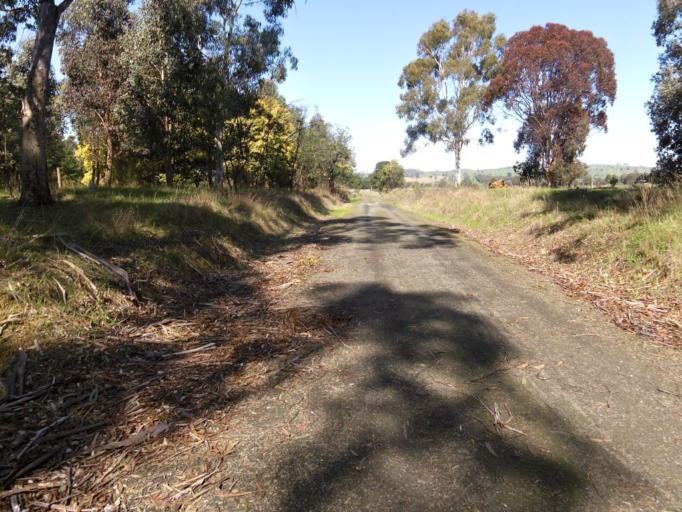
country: AU
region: Victoria
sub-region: Murrindindi
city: Alexandra
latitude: -37.0020
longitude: 145.7467
